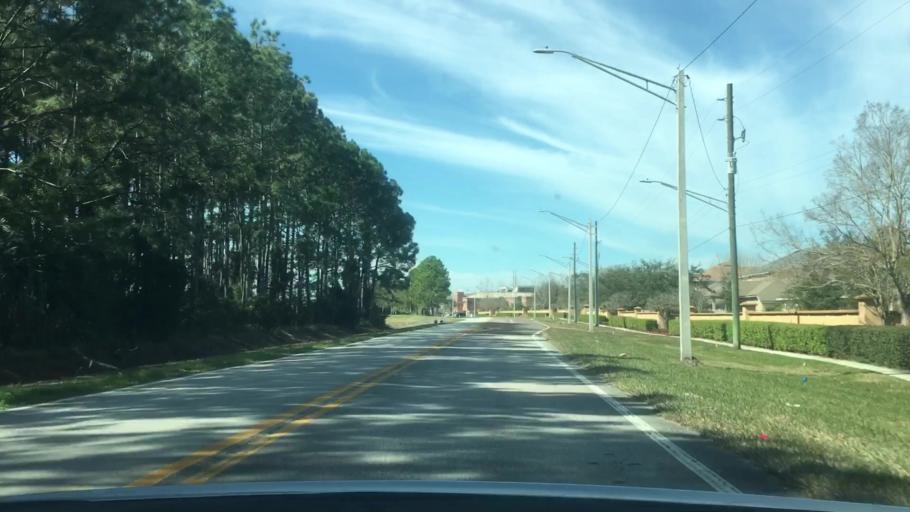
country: US
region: Florida
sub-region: Duval County
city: Atlantic Beach
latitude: 30.3217
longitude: -81.4829
